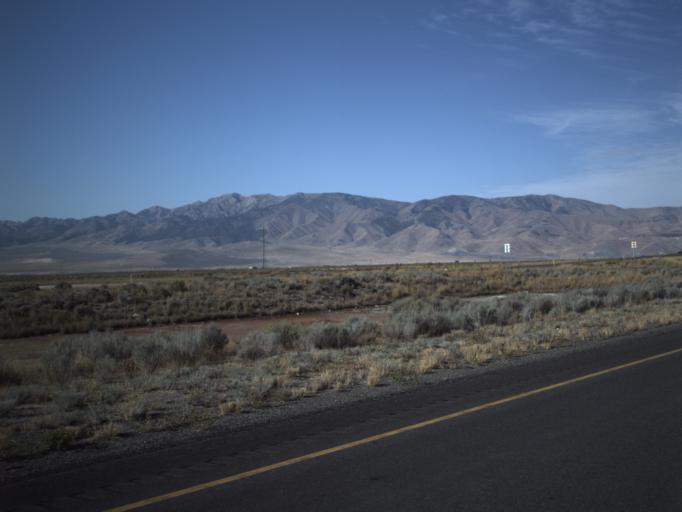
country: US
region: Utah
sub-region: Tooele County
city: Grantsville
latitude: 40.6831
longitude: -112.4334
